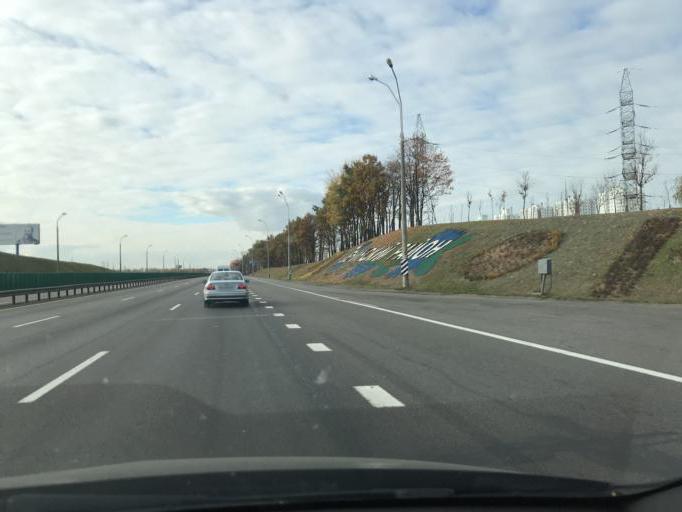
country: BY
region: Minsk
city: Machulishchy
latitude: 53.8334
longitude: 27.5988
